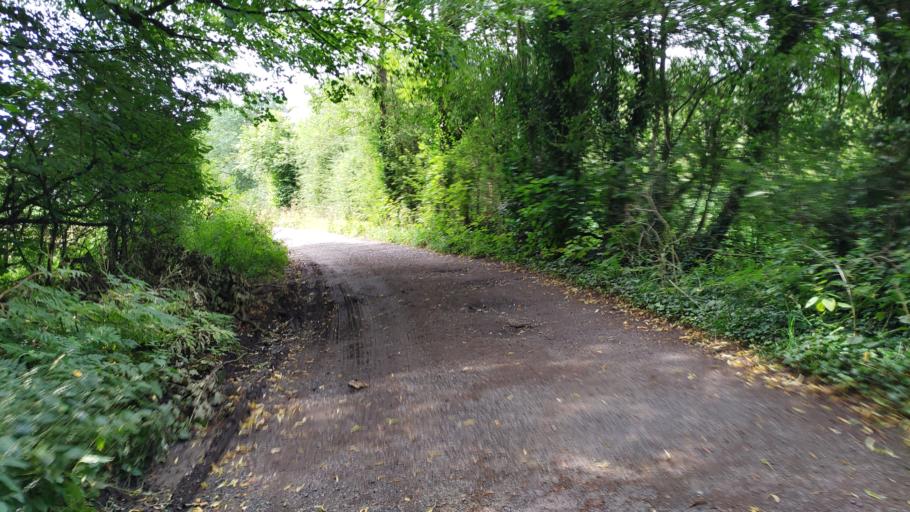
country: GB
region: England
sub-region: Lancashire
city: Coppull
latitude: 53.6337
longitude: -2.6394
